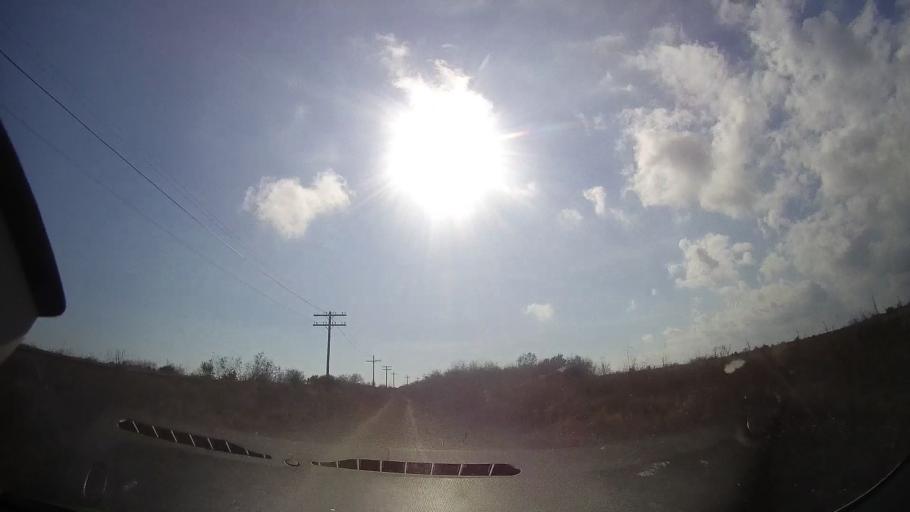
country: RO
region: Constanta
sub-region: Comuna Tuzla
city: Tuzla
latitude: 43.9905
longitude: 28.6450
